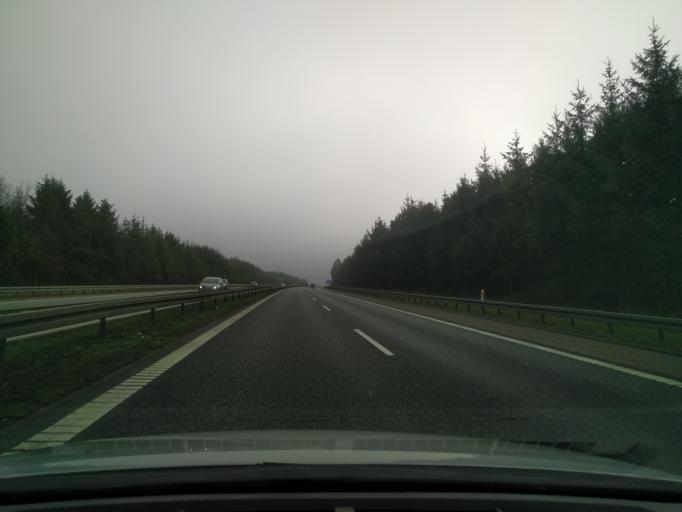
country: DK
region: Zealand
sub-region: Ringsted Kommune
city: Ringsted
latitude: 55.4538
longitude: 11.7840
